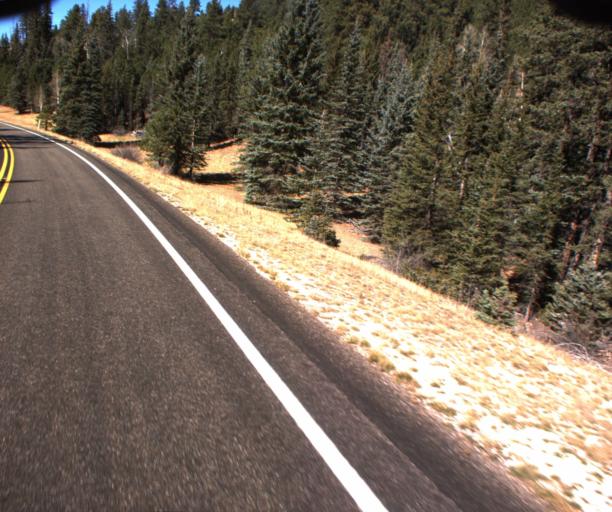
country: US
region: Arizona
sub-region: Coconino County
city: Grand Canyon
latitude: 36.5220
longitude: -112.1398
